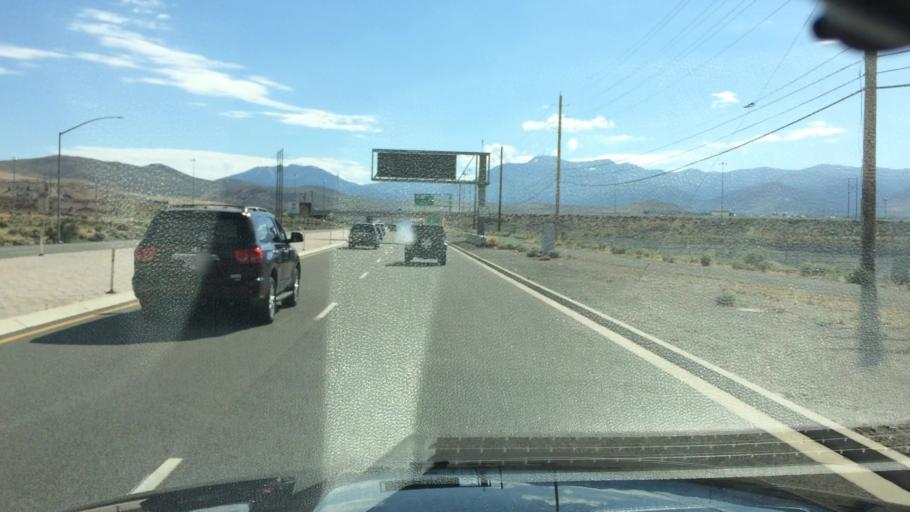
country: US
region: Nevada
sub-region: Washoe County
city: Sparks
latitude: 39.3995
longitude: -119.7533
